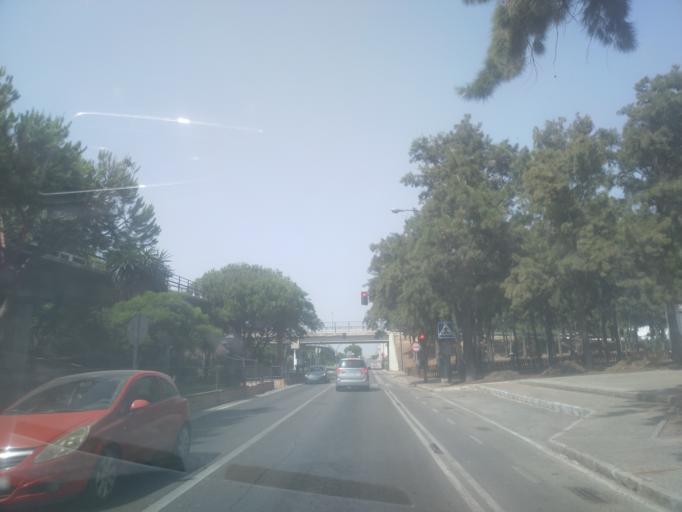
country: ES
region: Andalusia
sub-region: Provincia de Cadiz
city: San Fernando
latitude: 36.4627
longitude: -6.2093
